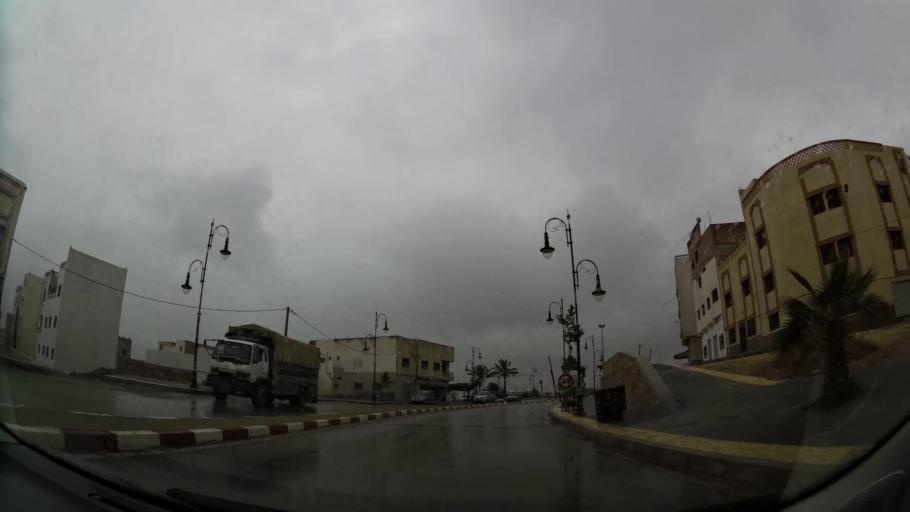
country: MA
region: Taza-Al Hoceima-Taounate
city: Imzourene
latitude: 35.1540
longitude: -3.8441
